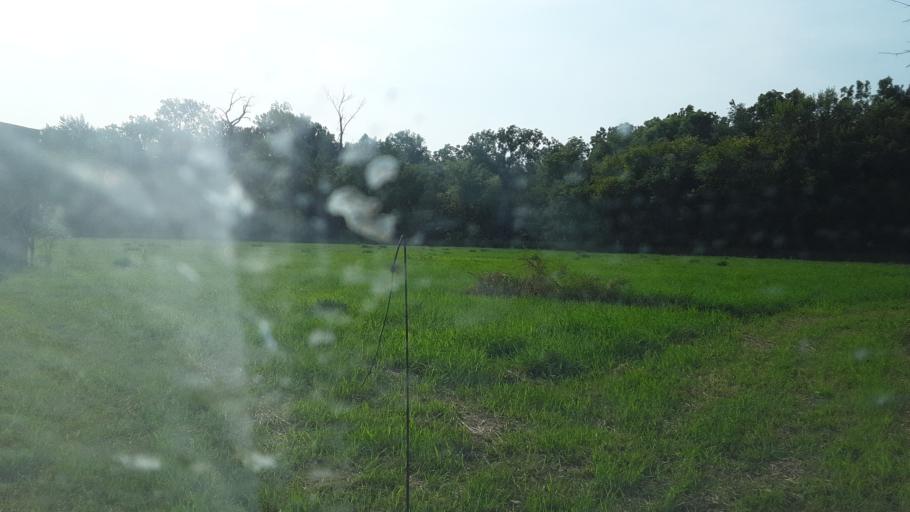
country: US
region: Ohio
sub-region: Crawford County
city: Bucyrus
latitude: 40.6597
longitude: -82.9551
